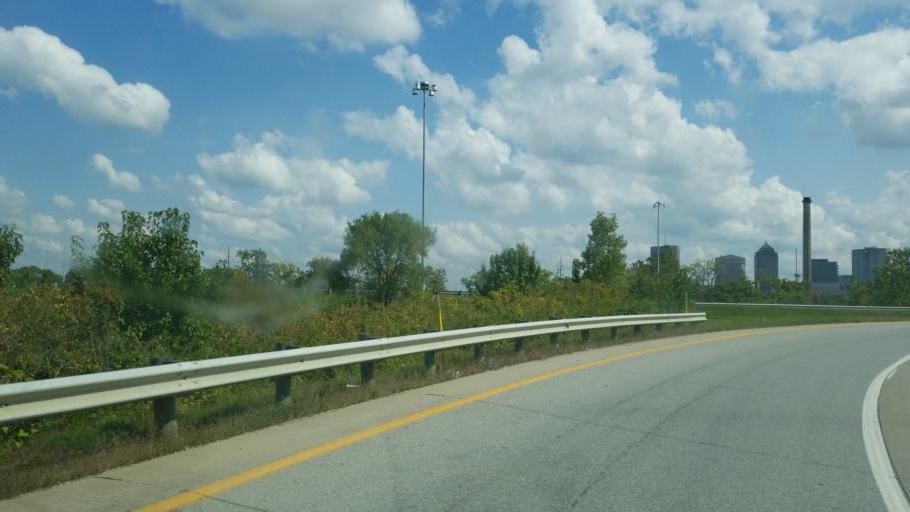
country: US
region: Ohio
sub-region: Franklin County
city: Grandview Heights
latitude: 39.9672
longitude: -83.0228
